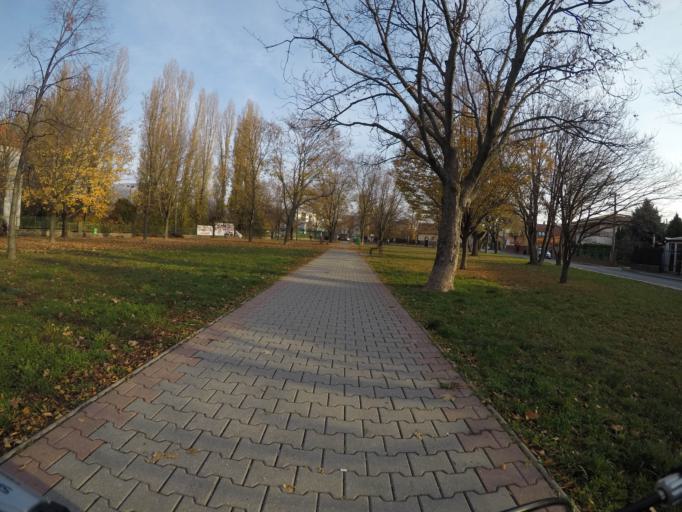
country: SK
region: Bratislavsky
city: Bratislava
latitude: 48.1699
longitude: 17.1687
